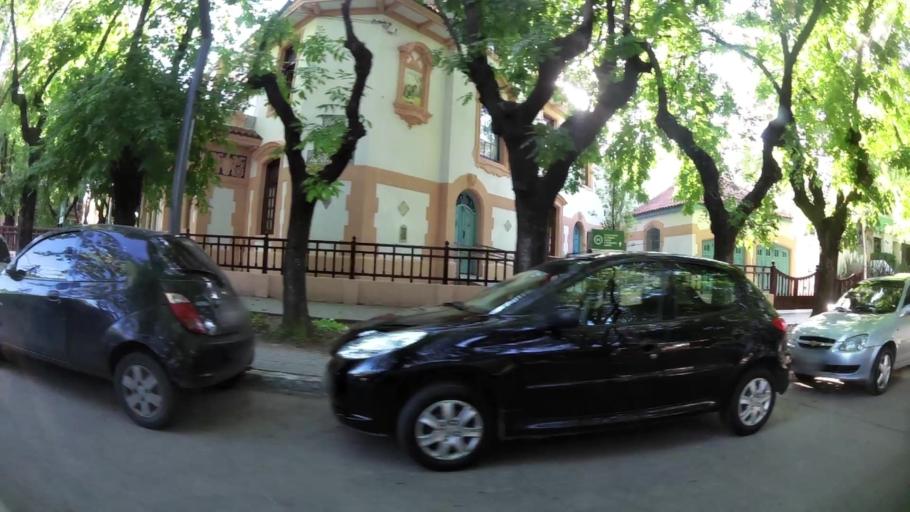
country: AR
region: Buenos Aires
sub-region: Partido de Merlo
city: Merlo
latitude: -34.6724
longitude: -58.7254
